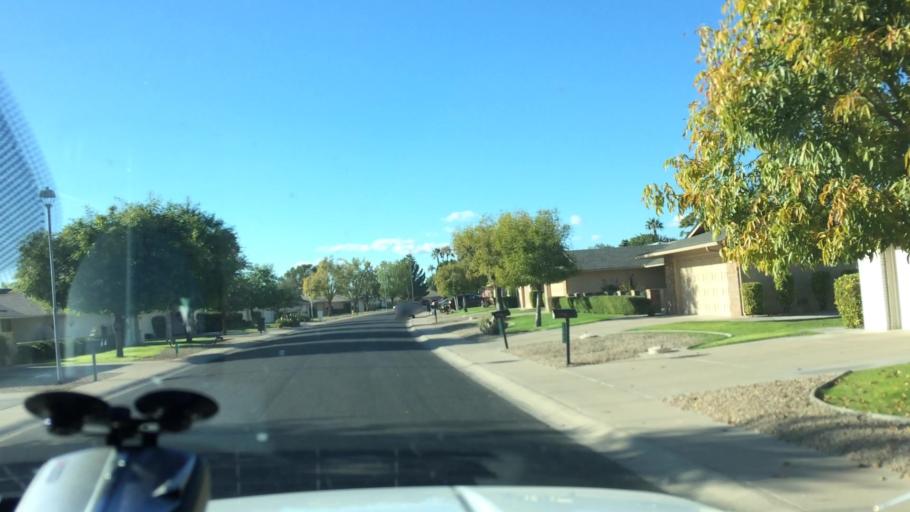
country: US
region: Arizona
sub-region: Maricopa County
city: Sun City West
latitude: 33.6545
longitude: -112.3352
